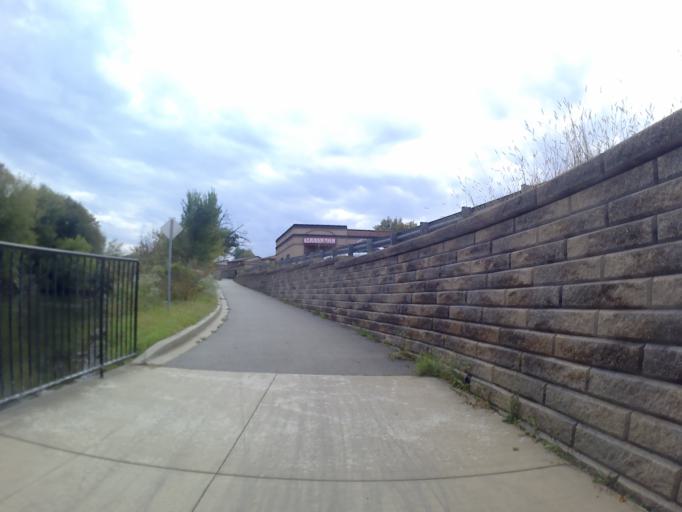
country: US
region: Illinois
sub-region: DuPage County
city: Naperville
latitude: 41.7816
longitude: -88.1753
